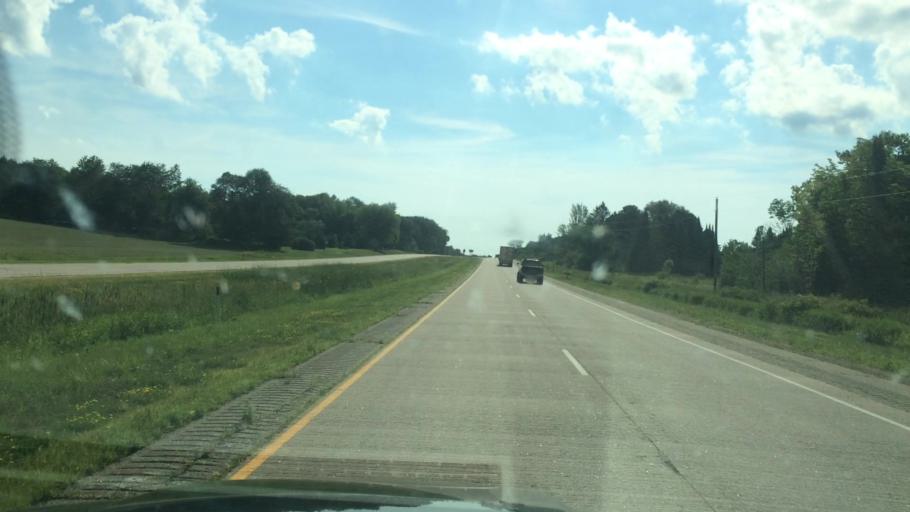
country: US
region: Wisconsin
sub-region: Waupaca County
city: Marion
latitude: 44.8040
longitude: -88.9862
